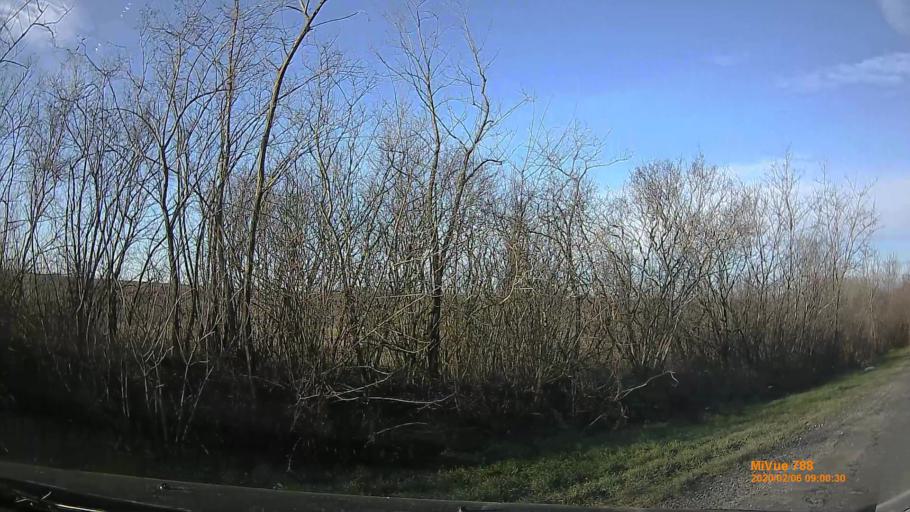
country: HU
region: Fejer
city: Etyek
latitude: 47.4930
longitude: 18.7588
